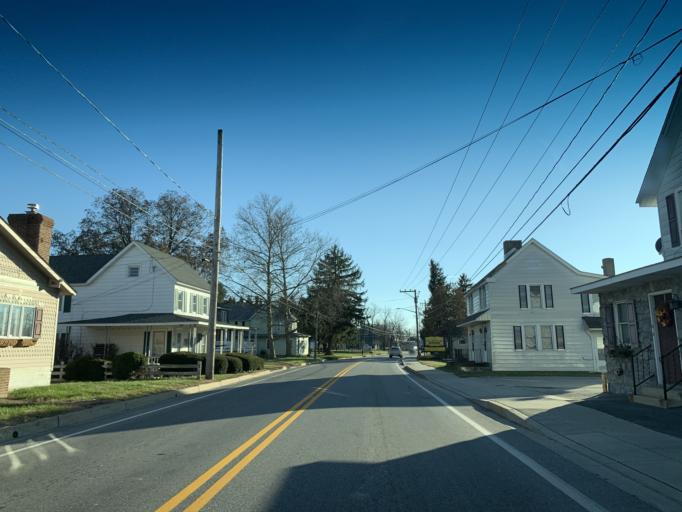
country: US
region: Delaware
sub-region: New Castle County
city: Middletown
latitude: 39.4036
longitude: -75.8679
